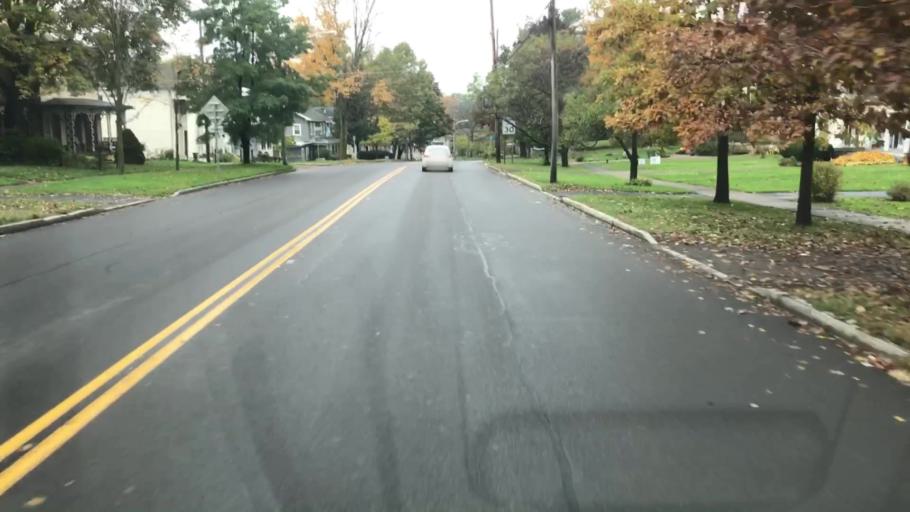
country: US
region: New York
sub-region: Onondaga County
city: Fayetteville
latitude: 43.0295
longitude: -76.0076
